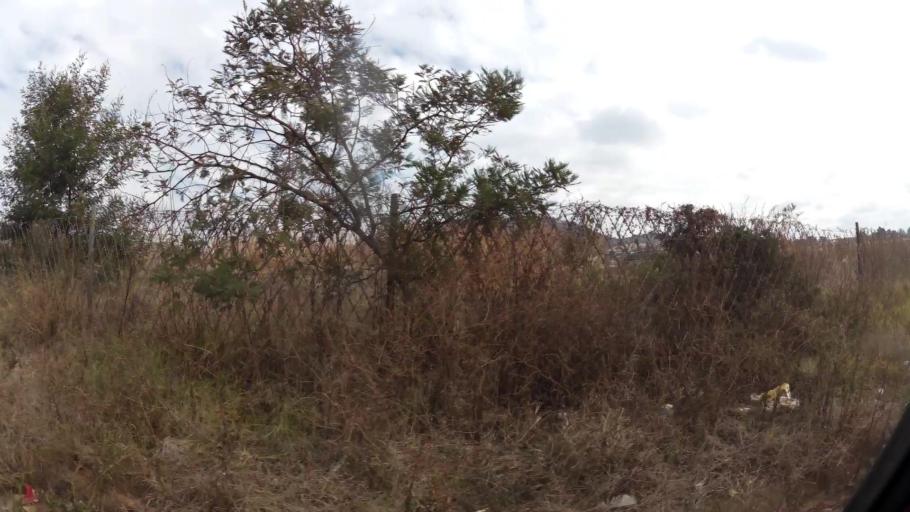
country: ZA
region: Gauteng
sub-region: City of Johannesburg Metropolitan Municipality
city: Roodepoort
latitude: -26.1063
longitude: 27.8857
